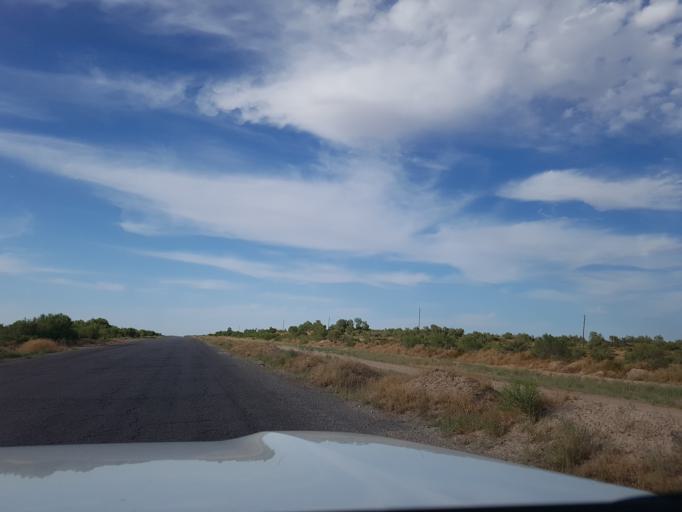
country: TM
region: Mary
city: Bayramaly
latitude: 37.8280
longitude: 62.5811
